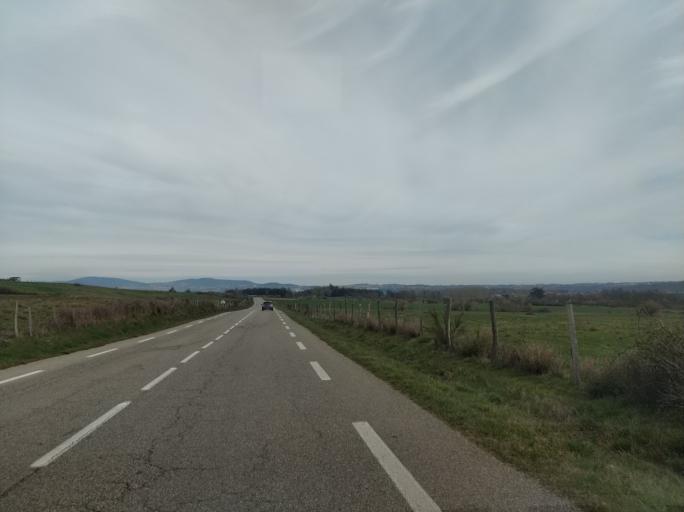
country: FR
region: Rhone-Alpes
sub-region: Departement de l'Ardeche
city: Roiffieux
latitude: 45.1999
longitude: 4.6546
